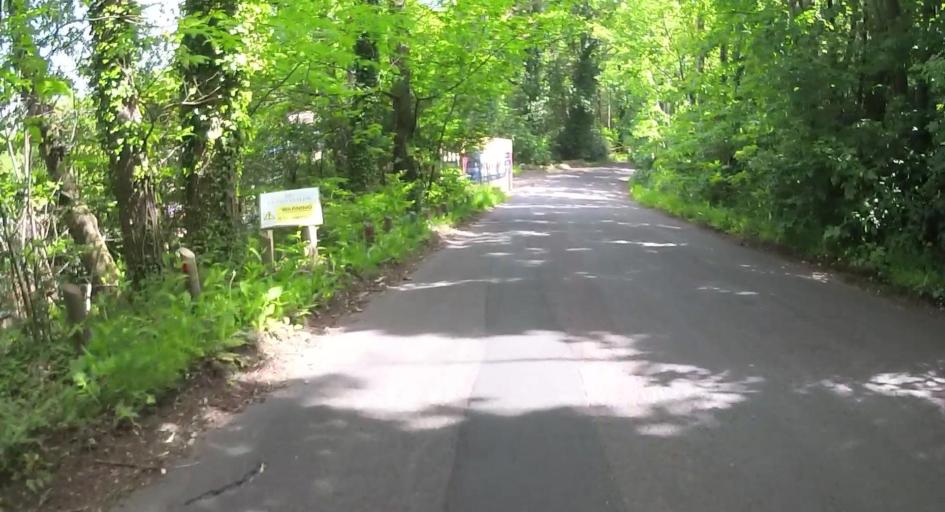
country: GB
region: England
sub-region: Surrey
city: Farnham
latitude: 51.1877
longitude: -0.8027
